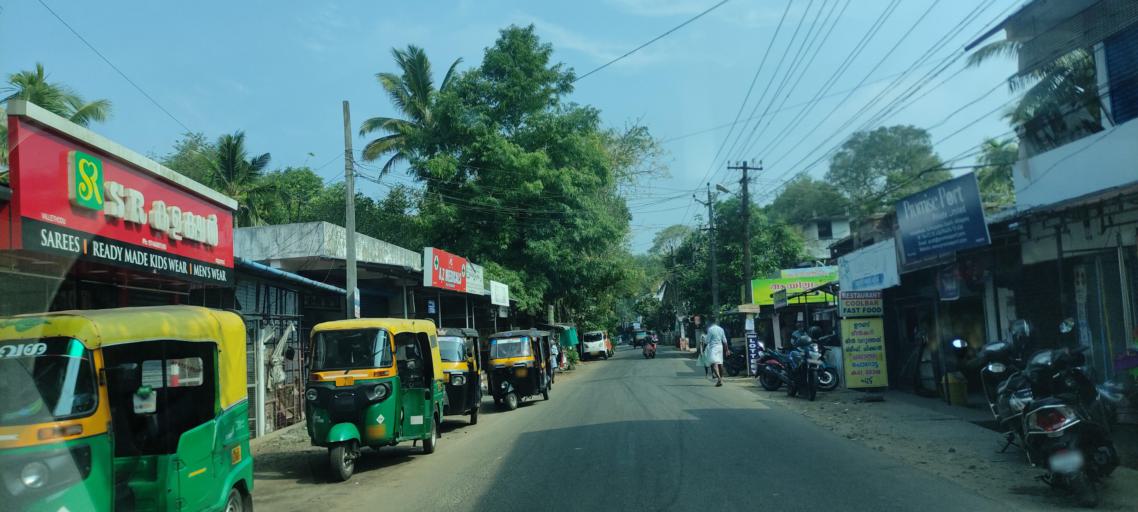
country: IN
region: Kerala
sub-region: Alappuzha
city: Kutiatodu
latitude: 9.7945
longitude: 76.3025
